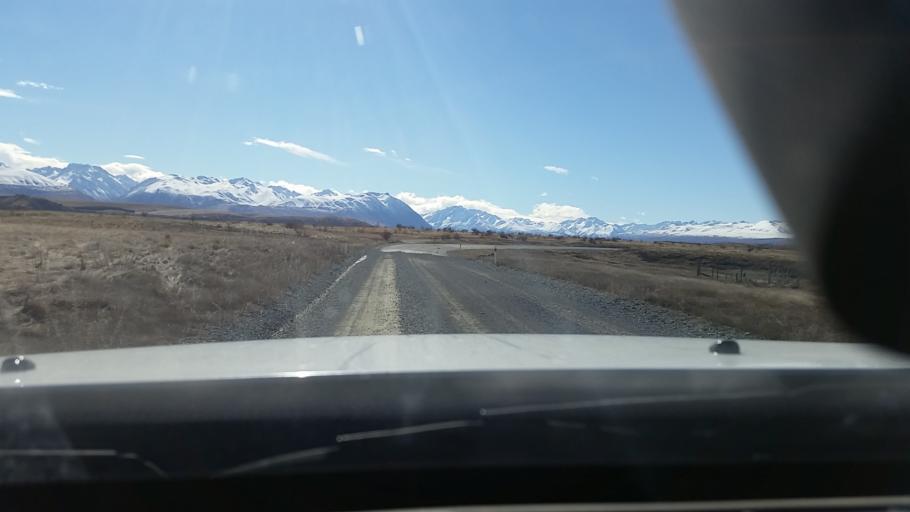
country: NZ
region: Canterbury
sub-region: Timaru District
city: Pleasant Point
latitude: -43.9945
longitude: 170.5000
